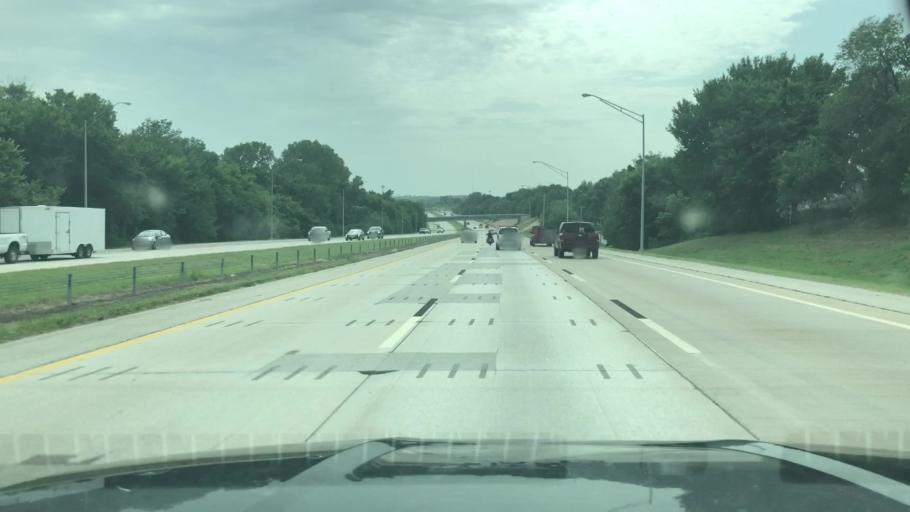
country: US
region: Oklahoma
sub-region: Tulsa County
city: Tulsa
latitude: 36.1583
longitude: -96.0331
